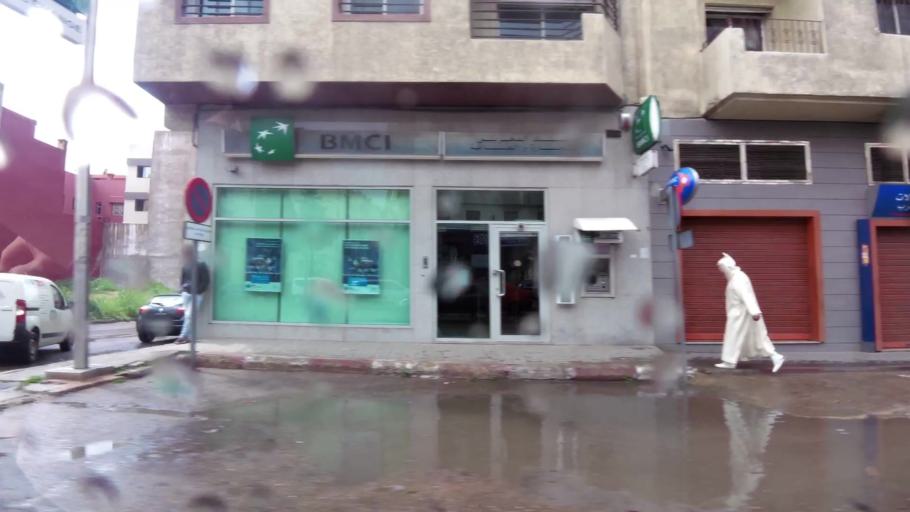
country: MA
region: Grand Casablanca
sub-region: Casablanca
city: Casablanca
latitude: 33.5308
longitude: -7.6485
